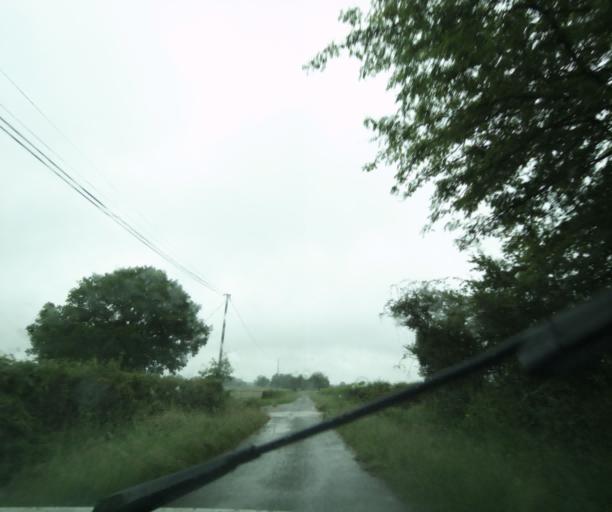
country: FR
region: Bourgogne
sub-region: Departement de Saone-et-Loire
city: Ciry-le-Noble
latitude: 46.5629
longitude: 4.3206
